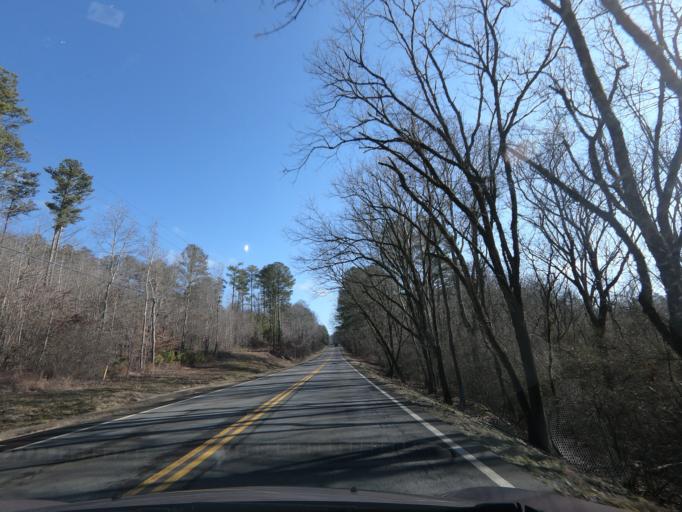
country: US
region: Georgia
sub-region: Cherokee County
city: Ball Ground
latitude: 34.2936
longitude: -84.2622
